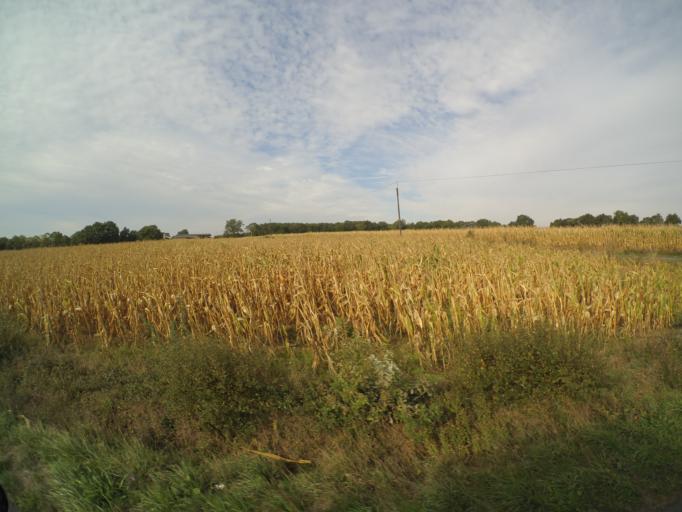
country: FR
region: Pays de la Loire
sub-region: Departement de Maine-et-Loire
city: Villedieu-la-Blouere
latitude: 47.1708
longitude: -1.0469
